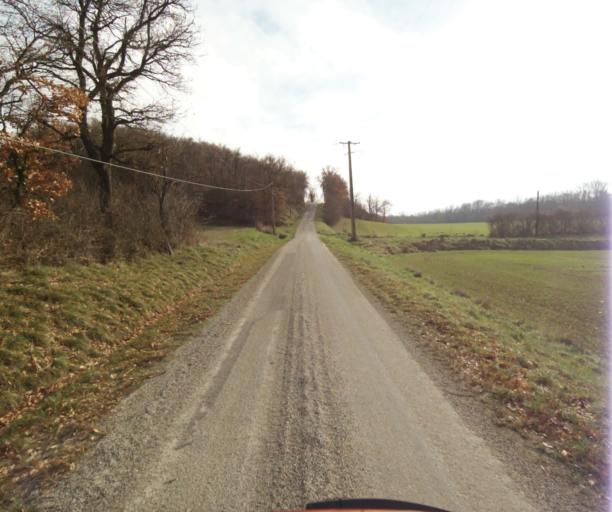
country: FR
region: Languedoc-Roussillon
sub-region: Departement de l'Aude
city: Belpech
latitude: 43.1698
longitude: 1.7378
